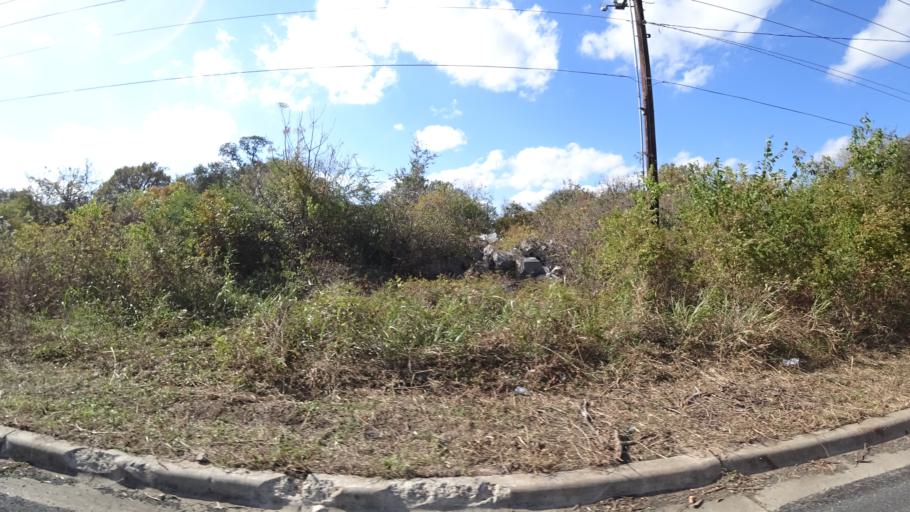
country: US
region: Texas
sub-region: Williamson County
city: Jollyville
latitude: 30.4159
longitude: -97.7293
